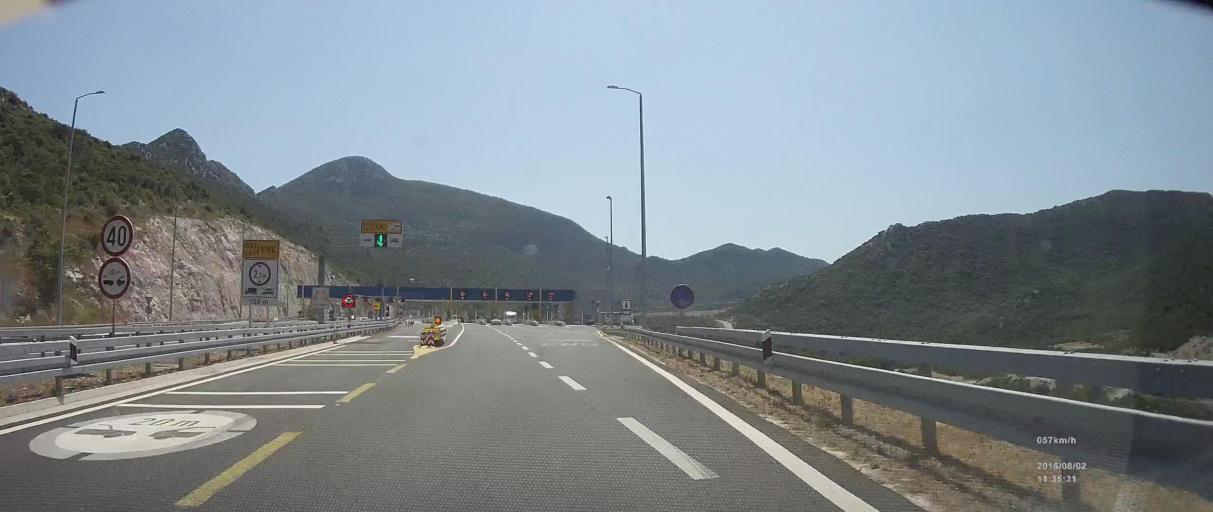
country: HR
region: Dubrovacko-Neretvanska
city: Komin
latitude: 43.1023
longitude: 17.4835
